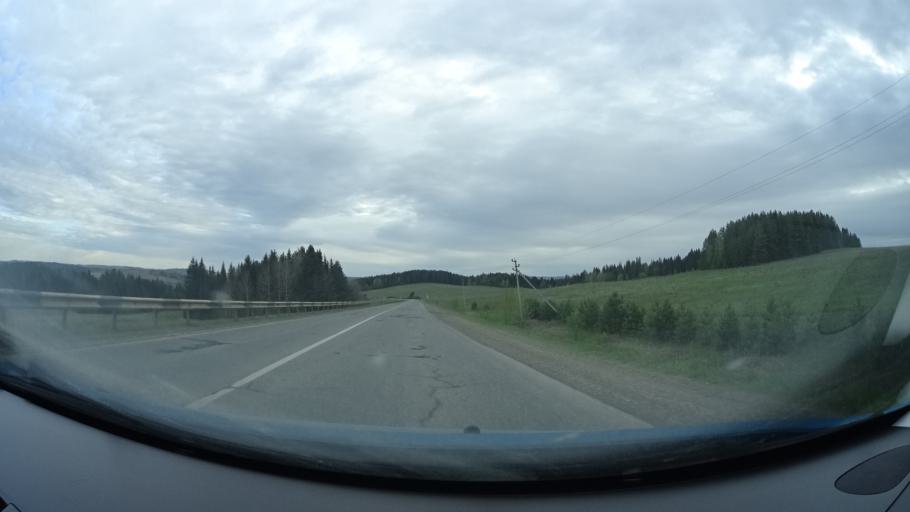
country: RU
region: Perm
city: Osa
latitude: 57.3143
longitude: 55.6232
